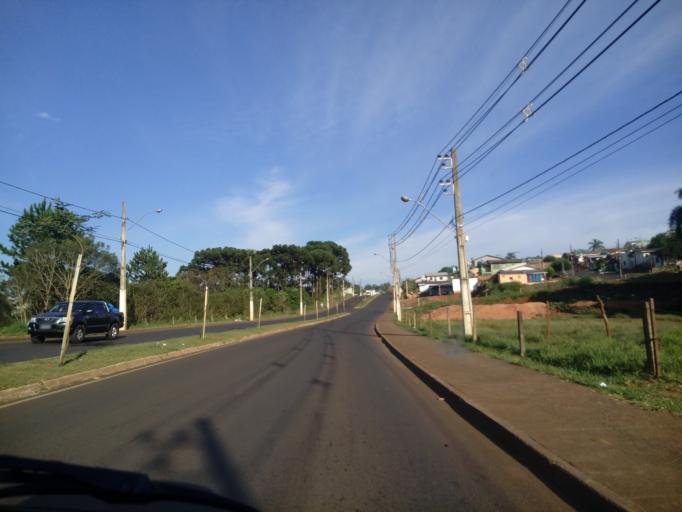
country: BR
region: Santa Catarina
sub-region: Chapeco
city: Chapeco
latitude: -27.0898
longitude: -52.6691
